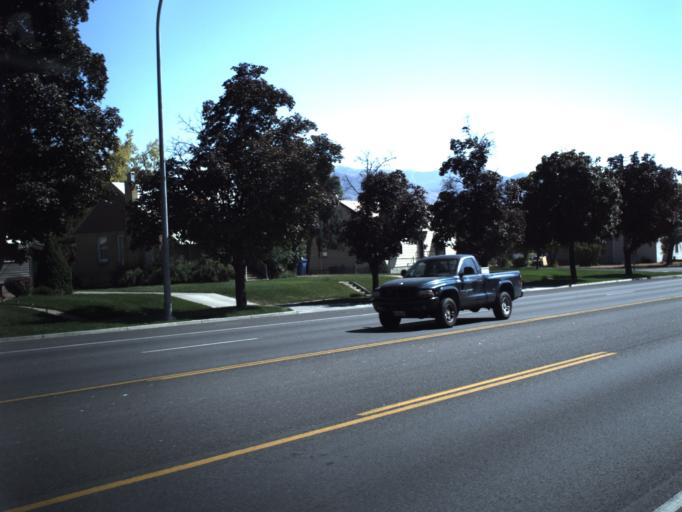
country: US
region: Utah
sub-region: Cache County
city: Smithfield
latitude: 41.8290
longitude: -111.8330
